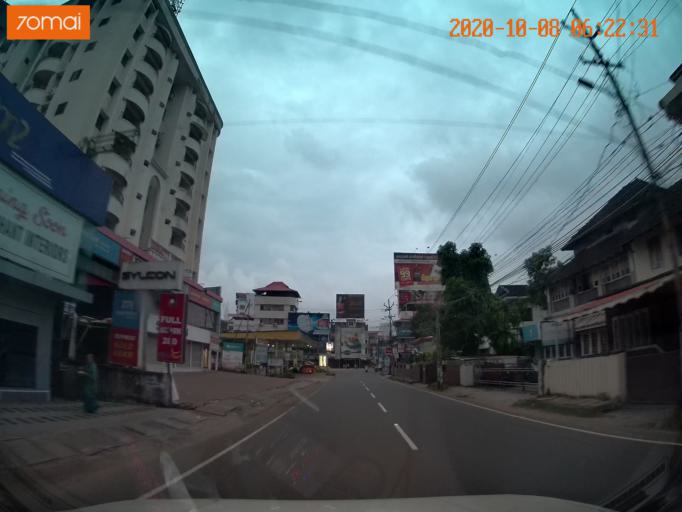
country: IN
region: Kerala
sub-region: Thrissur District
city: Trichur
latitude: 10.5231
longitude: 76.2229
